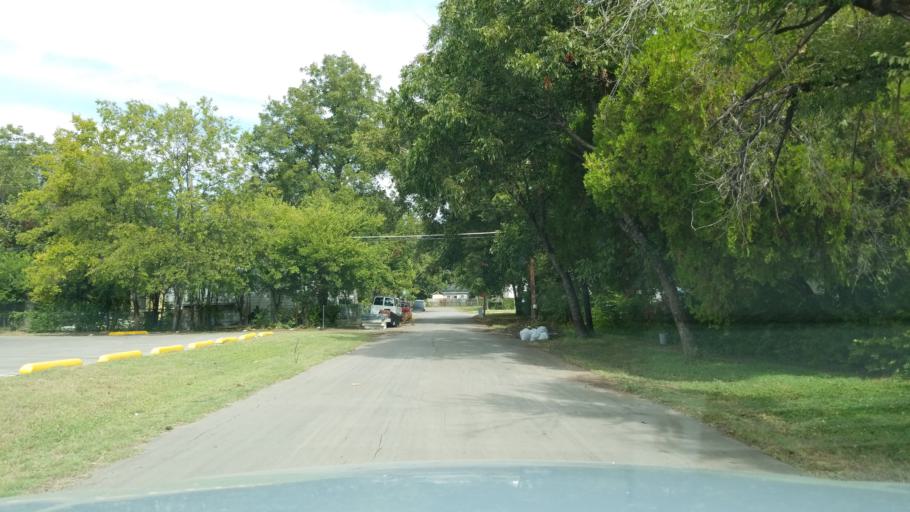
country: US
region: Texas
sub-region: Dallas County
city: Dallas
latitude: 32.7865
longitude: -96.7407
